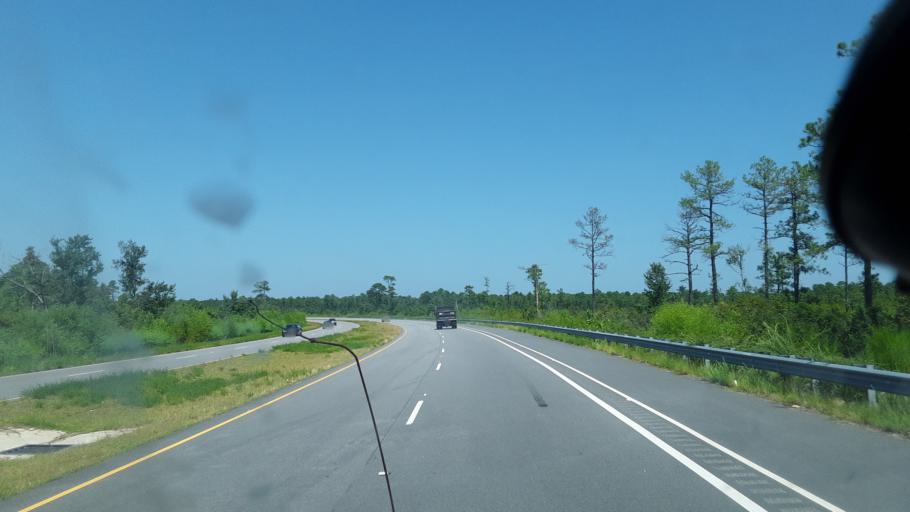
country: US
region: South Carolina
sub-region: Horry County
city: Forestbrook
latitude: 33.7978
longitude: -78.8828
